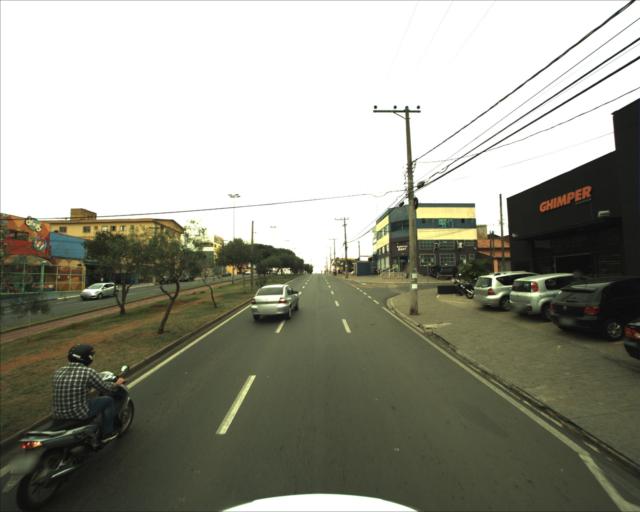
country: BR
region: Sao Paulo
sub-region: Sorocaba
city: Sorocaba
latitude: -23.4913
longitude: -47.5050
